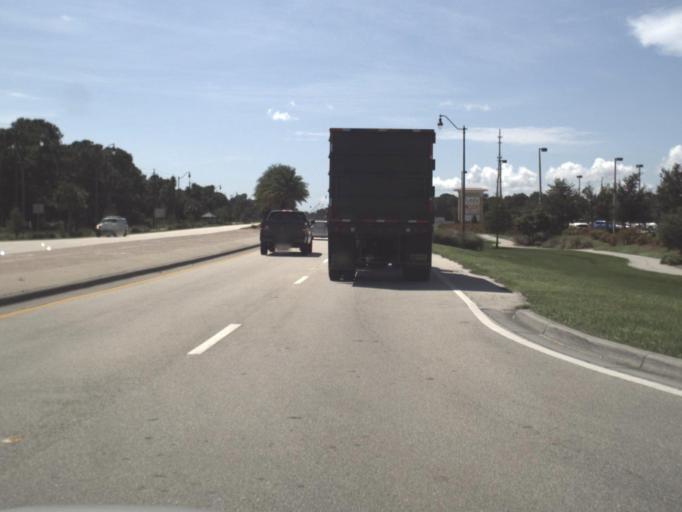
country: US
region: Florida
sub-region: Sarasota County
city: North Port
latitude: 27.0683
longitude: -82.1571
